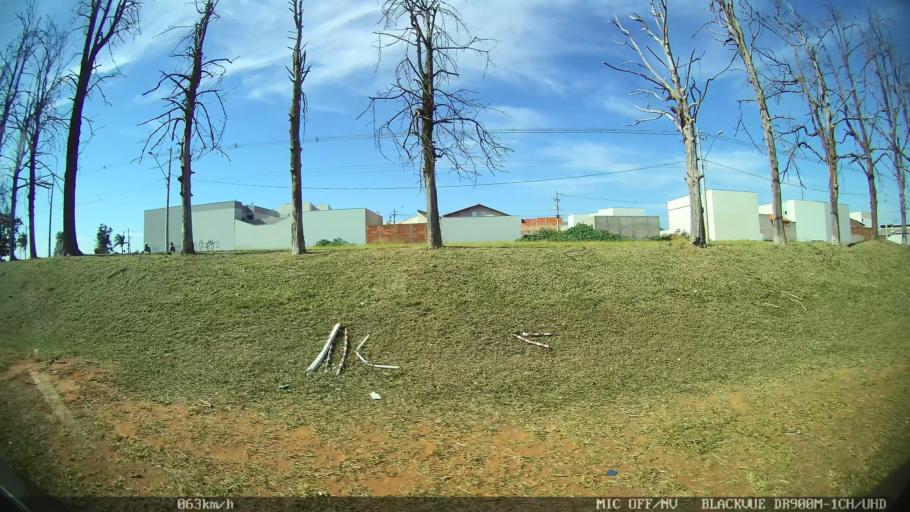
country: BR
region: Sao Paulo
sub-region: Franca
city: Franca
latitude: -20.5075
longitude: -47.4411
